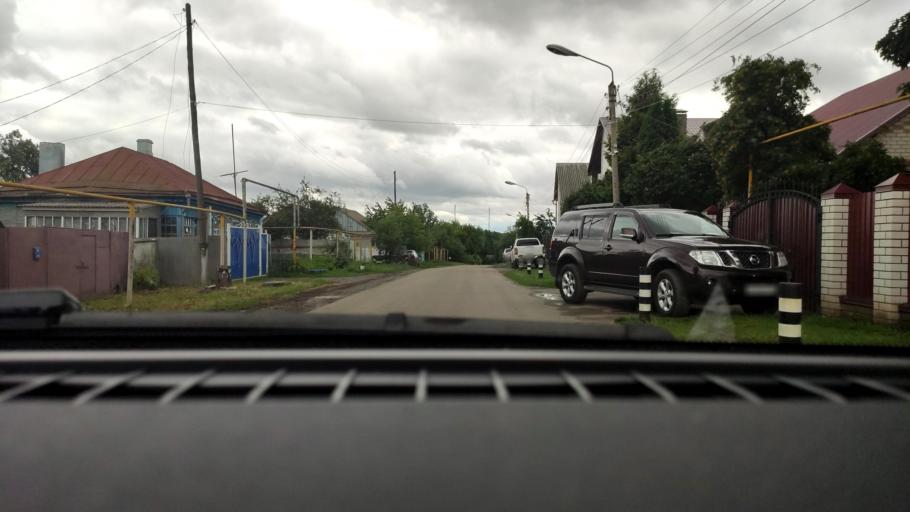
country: RU
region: Voronezj
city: Zemlyansk
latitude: 51.9039
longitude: 38.7330
